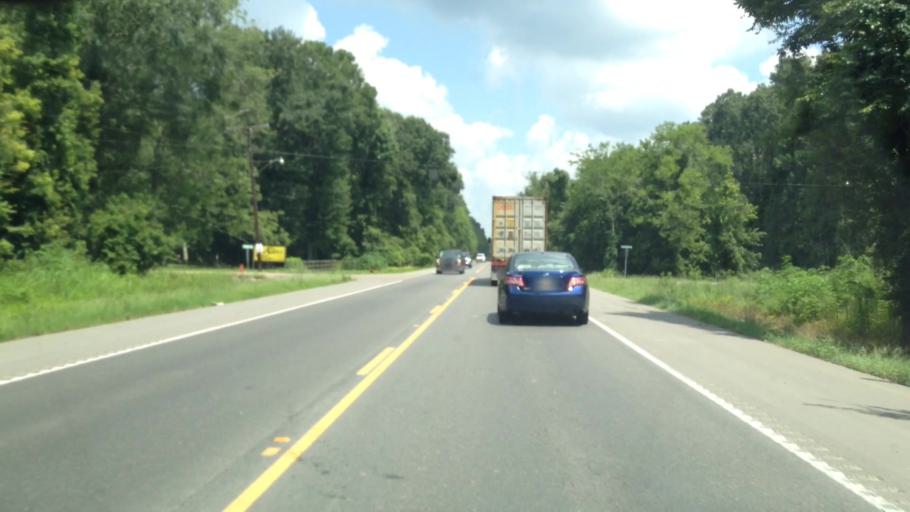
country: US
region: Louisiana
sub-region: Ascension Parish
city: Sorrento
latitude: 30.1561
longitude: -90.8763
